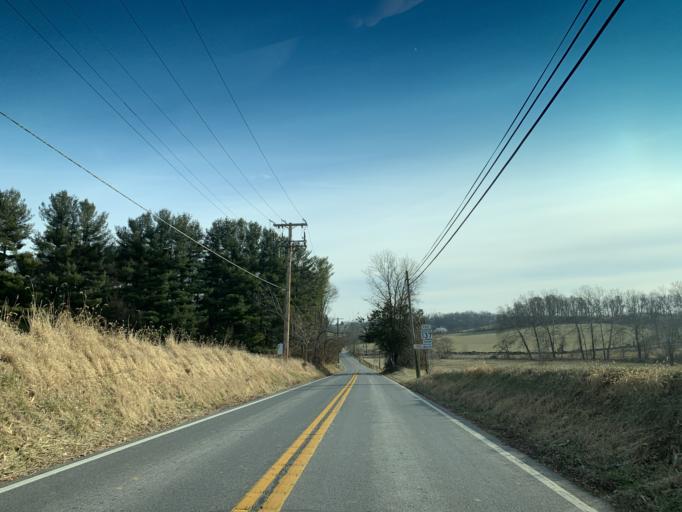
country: US
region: Maryland
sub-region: Carroll County
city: Hampstead
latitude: 39.6123
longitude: -76.7992
